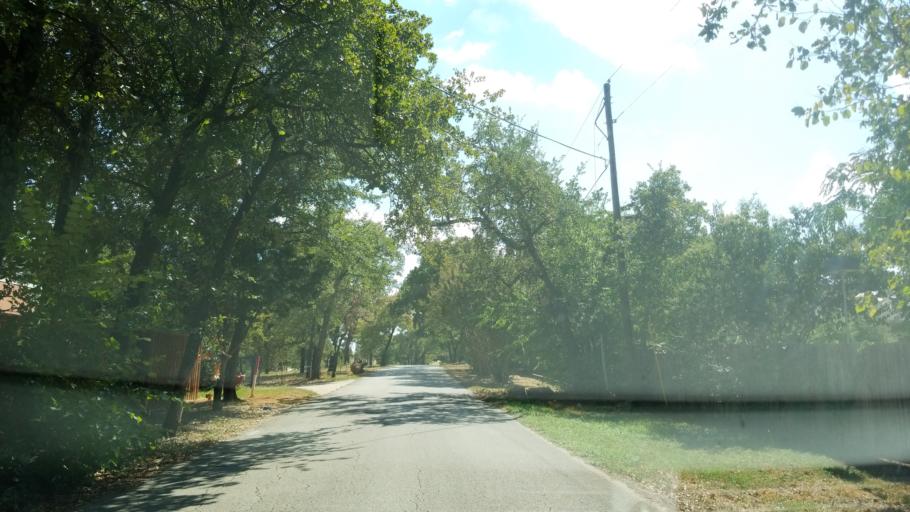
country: US
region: Texas
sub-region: Tarrant County
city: Euless
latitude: 32.8619
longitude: -97.1071
